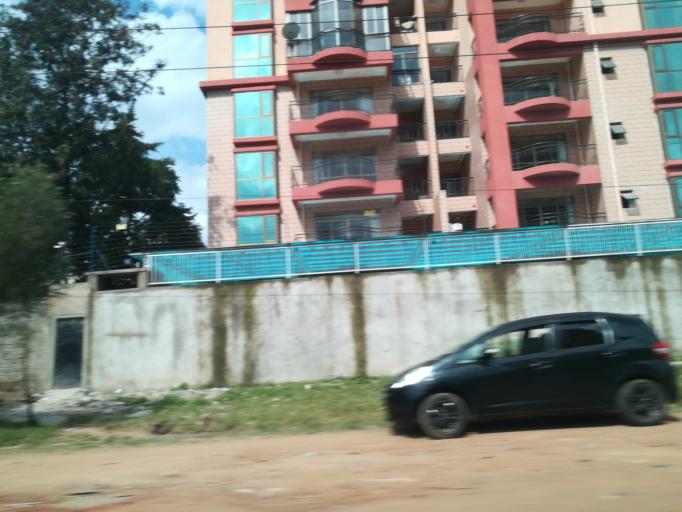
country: KE
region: Nairobi Area
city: Nairobi
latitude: -1.2878
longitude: 36.7873
